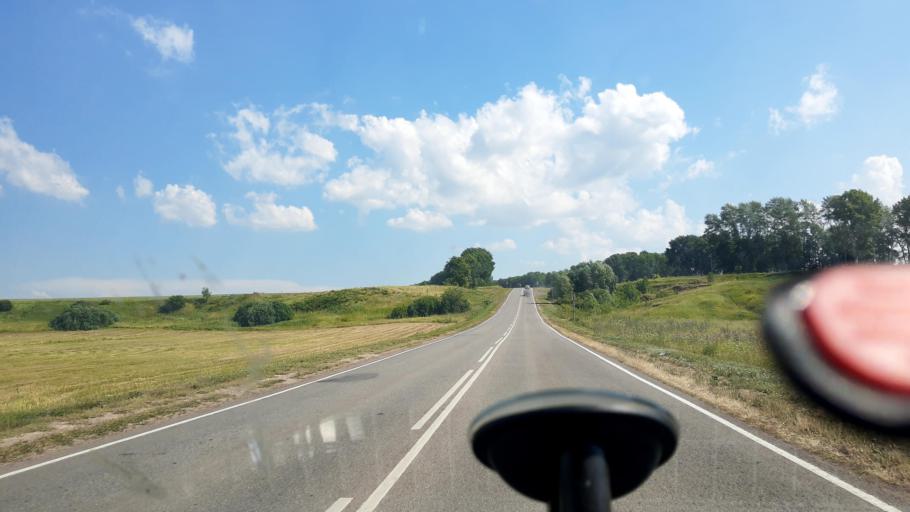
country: RU
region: Bashkortostan
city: Alekseyevka
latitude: 55.0682
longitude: 55.0918
